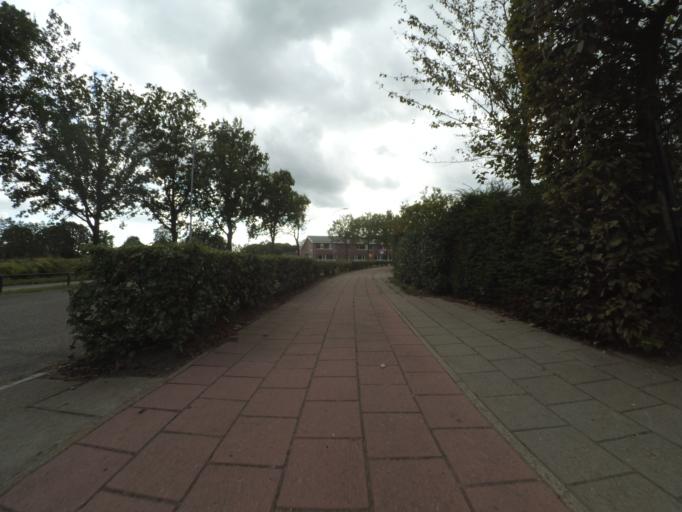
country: NL
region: Utrecht
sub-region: Gemeente Utrechtse Heuvelrug
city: Overberg
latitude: 52.0751
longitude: 5.4946
